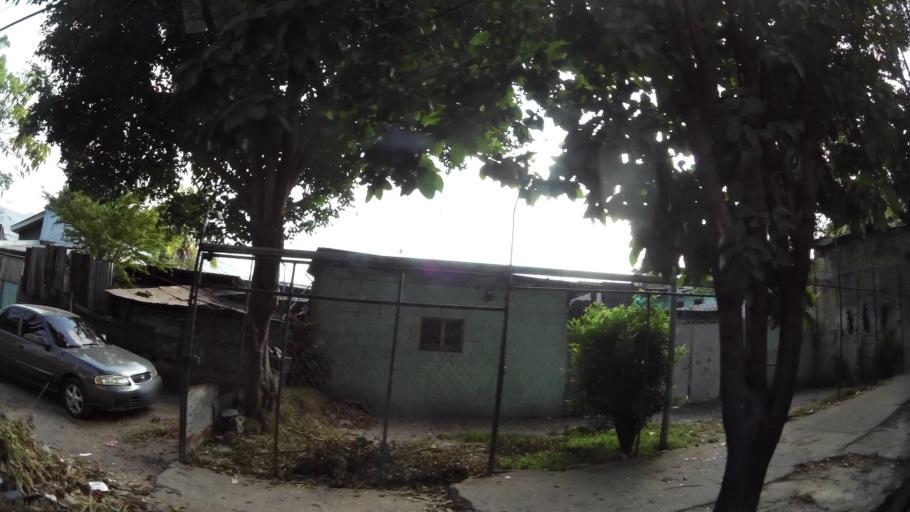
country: SV
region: San Salvador
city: San Salvador
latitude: 13.6958
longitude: -89.1816
